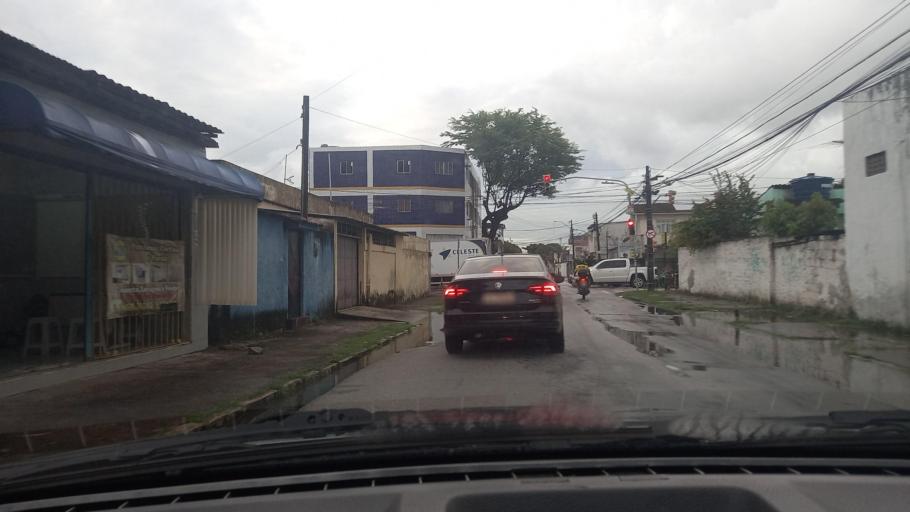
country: ET
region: Gambela
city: Gambela
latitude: 8.1072
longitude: 34.9258
